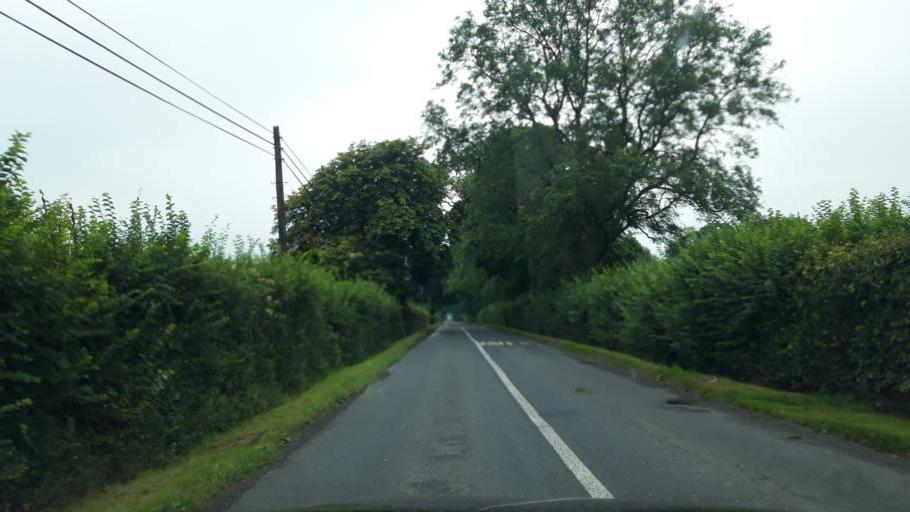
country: IE
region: Munster
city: Fethard
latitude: 52.5033
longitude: -7.6857
